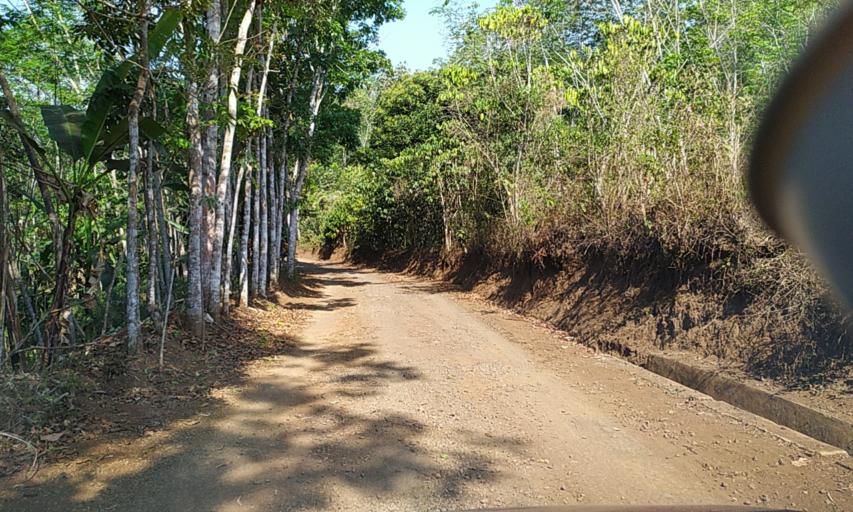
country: ID
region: Central Java
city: Datar
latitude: -7.2168
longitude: 108.6214
